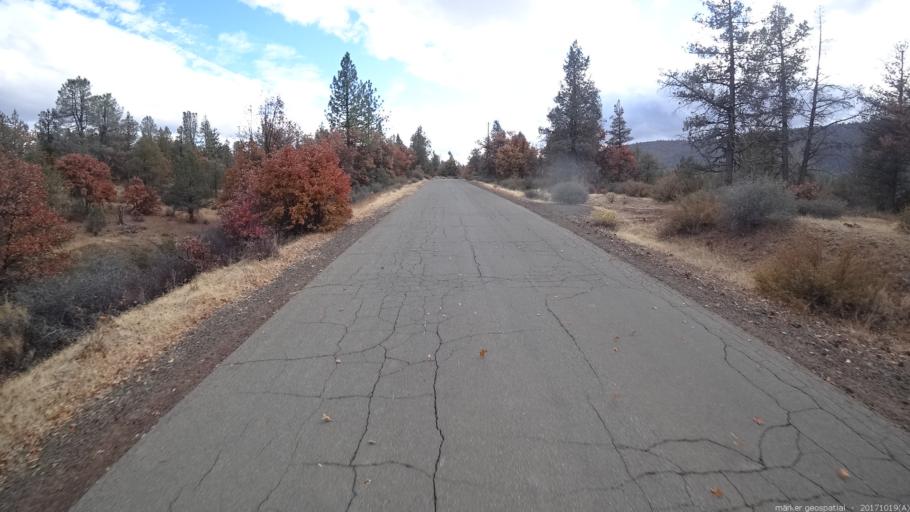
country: US
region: California
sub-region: Shasta County
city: Burney
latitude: 40.9758
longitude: -121.4457
